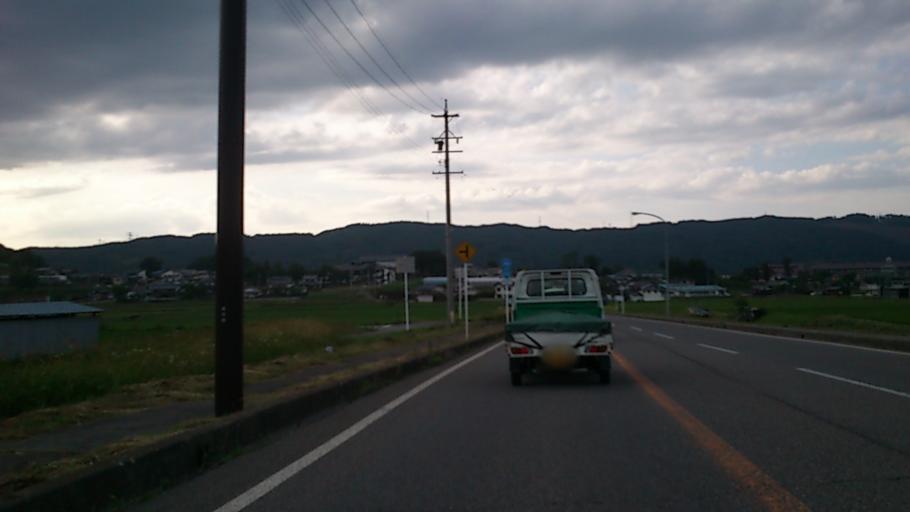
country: JP
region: Nagano
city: Komoro
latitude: 36.2633
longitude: 138.4016
